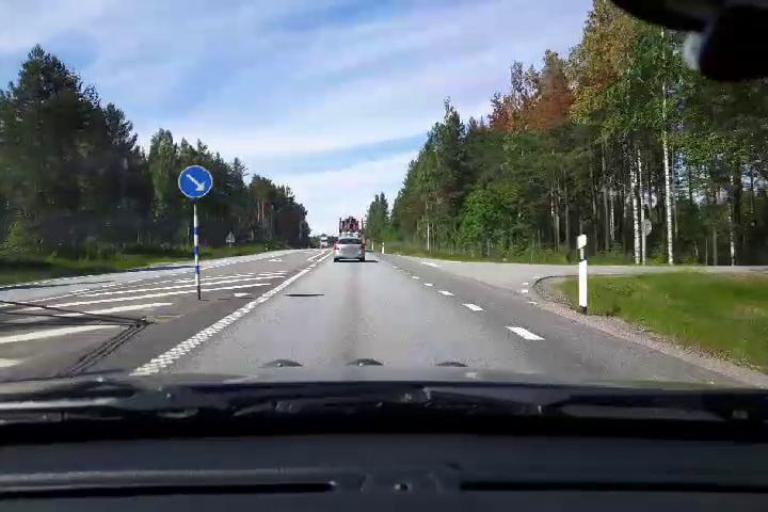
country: SE
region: Gaevleborg
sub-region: Gavle Kommun
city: Norrsundet
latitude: 61.0102
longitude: 16.9829
